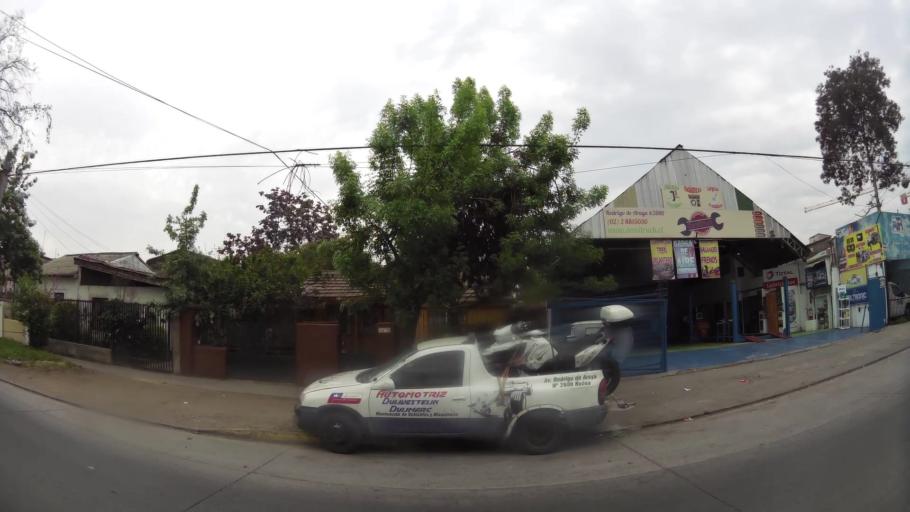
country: CL
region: Santiago Metropolitan
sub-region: Provincia de Santiago
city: Villa Presidente Frei, Nunoa, Santiago, Chile
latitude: -33.4739
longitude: -70.6017
